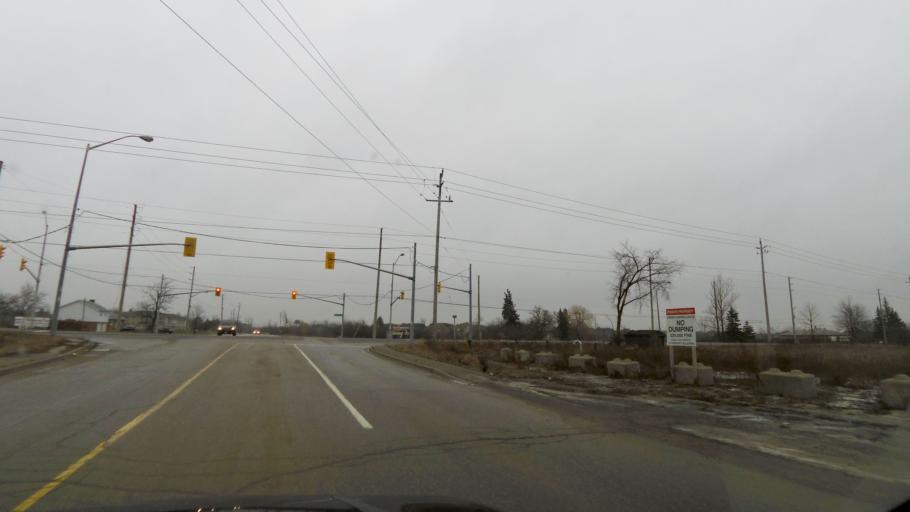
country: CA
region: Ontario
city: Brampton
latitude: 43.8008
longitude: -79.7494
